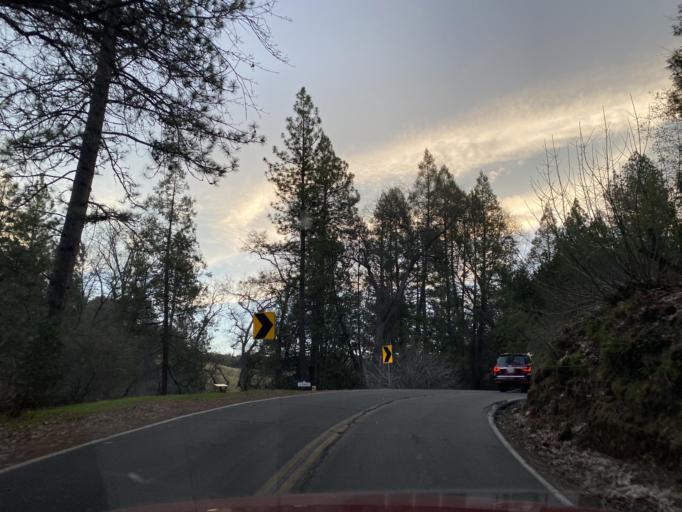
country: US
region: California
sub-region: Amador County
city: Pine Grove
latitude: 38.4984
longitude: -120.6978
